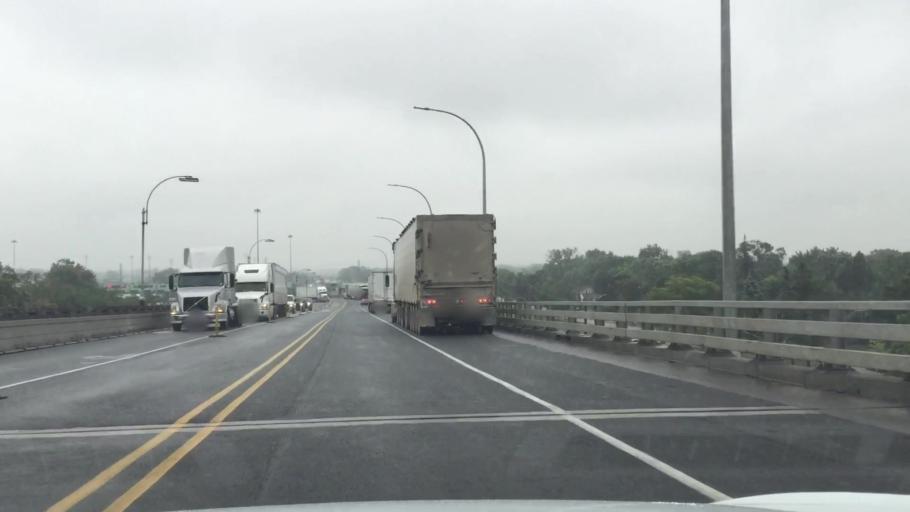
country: US
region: Michigan
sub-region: Wayne County
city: Detroit
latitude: 42.3045
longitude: -83.0693
